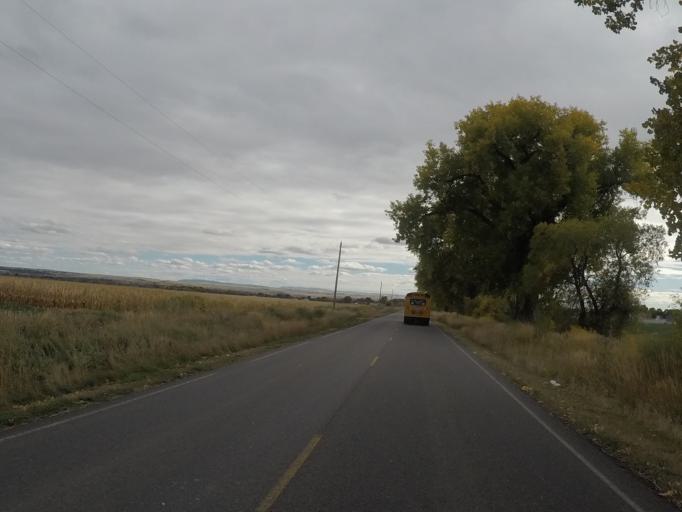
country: US
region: Montana
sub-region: Yellowstone County
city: Laurel
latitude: 45.7525
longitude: -108.6589
